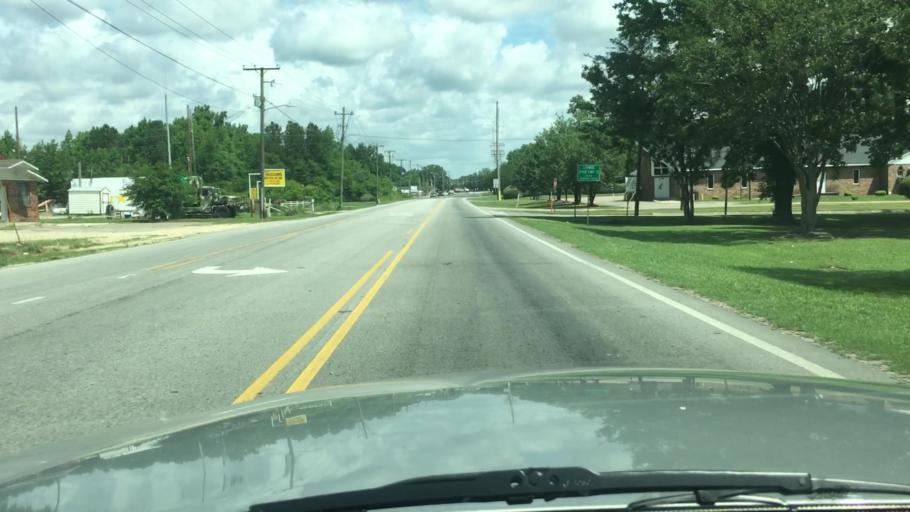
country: US
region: North Carolina
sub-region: Cumberland County
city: Fayetteville
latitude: 35.0304
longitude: -78.8721
